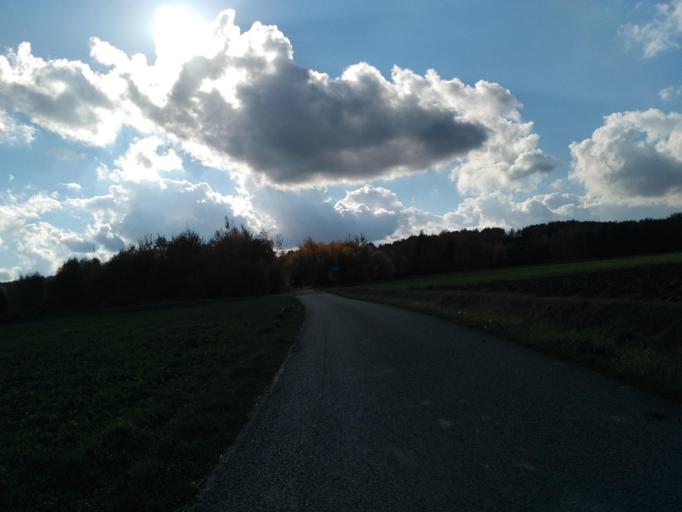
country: PL
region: Subcarpathian Voivodeship
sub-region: Powiat rzeszowski
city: Zglobien
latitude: 49.9888
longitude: 21.8456
